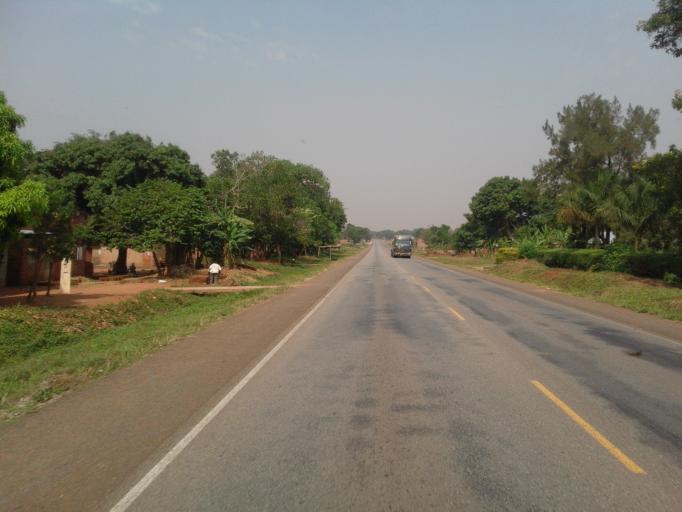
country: UG
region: Eastern Region
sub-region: Bugiri District
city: Bugiri
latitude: 0.6154
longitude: 33.6548
